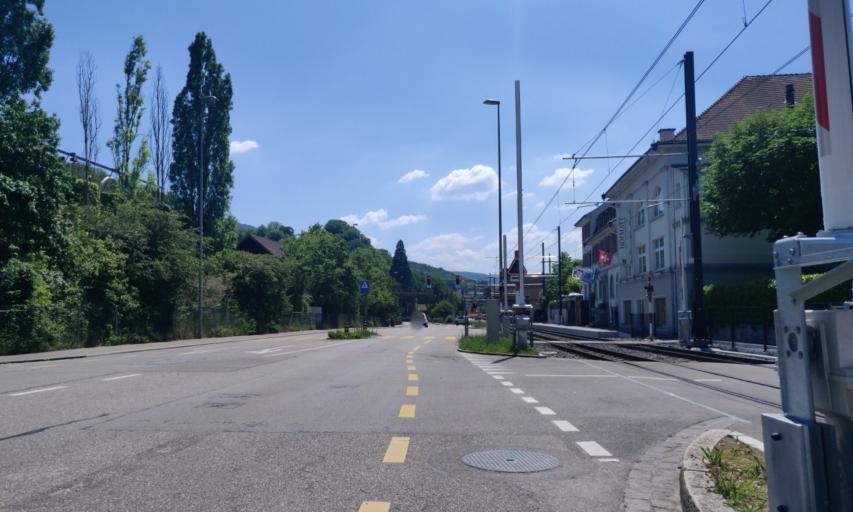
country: CH
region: Basel-Landschaft
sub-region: Bezirk Arlesheim
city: Munchenstein
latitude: 47.5204
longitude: 7.6182
